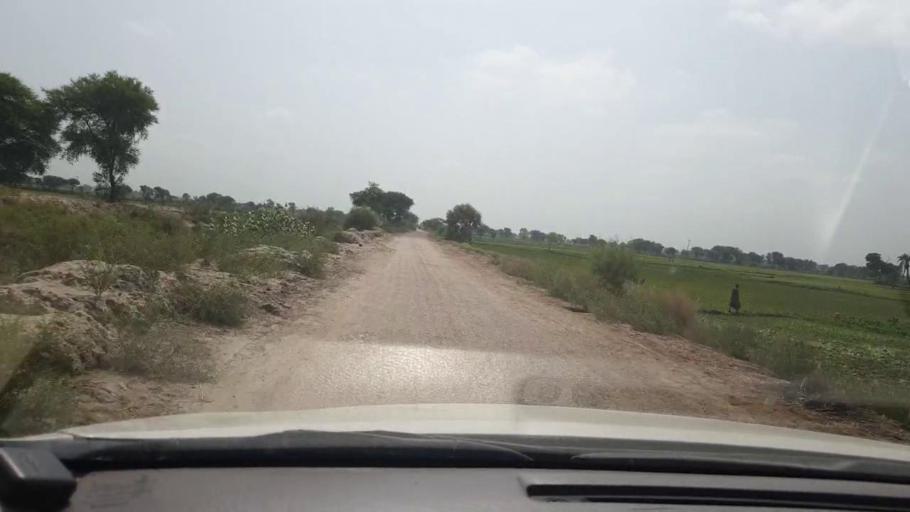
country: PK
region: Sindh
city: Shikarpur
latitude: 28.0083
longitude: 68.5739
